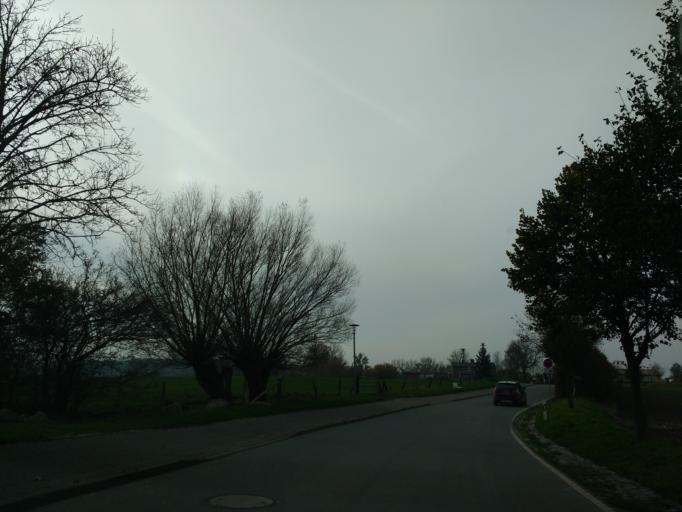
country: DE
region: Mecklenburg-Vorpommern
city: Ostseebad Boltenhagen
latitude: 53.9961
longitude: 11.1871
